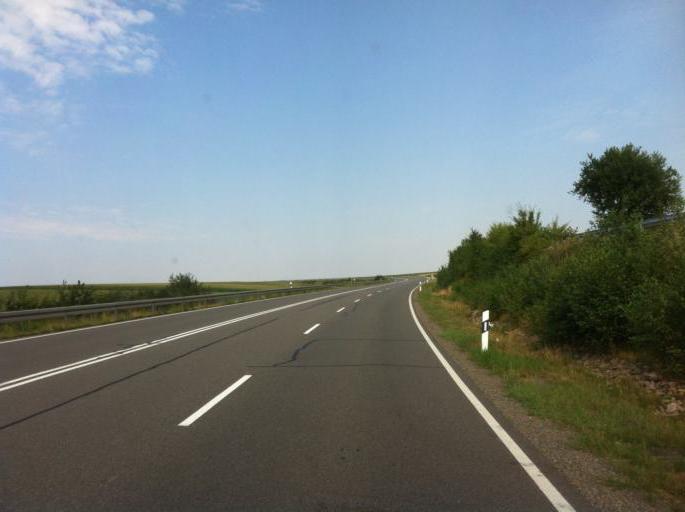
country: DE
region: Saxony
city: Reichenbach/Vogtland
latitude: 50.6140
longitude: 12.3224
